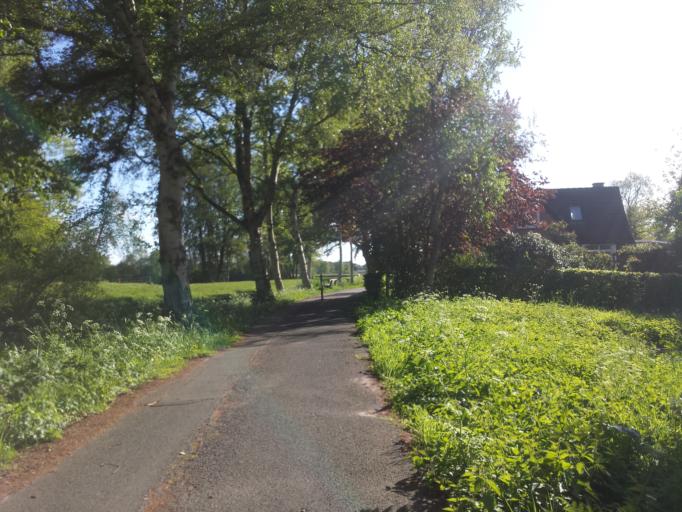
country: DE
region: Lower Saxony
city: Lilienthal
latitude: 53.1504
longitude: 8.9285
